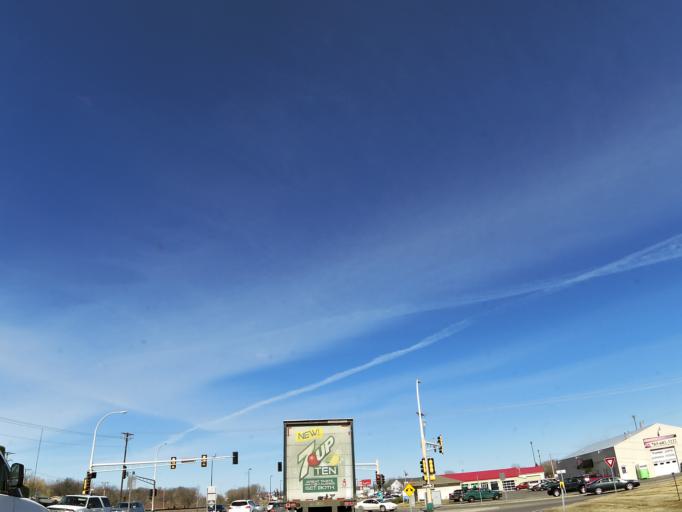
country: US
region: Minnesota
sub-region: Wright County
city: Buffalo
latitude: 45.1682
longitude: -93.8601
